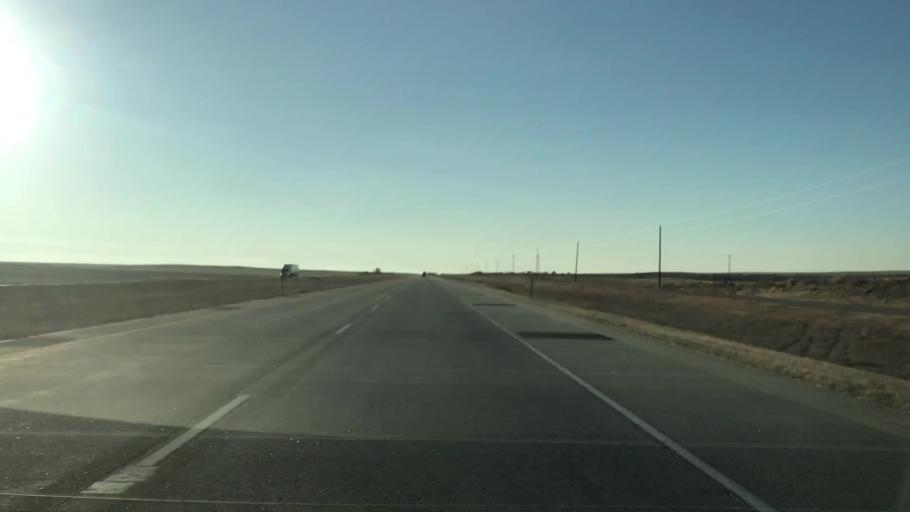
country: US
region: Colorado
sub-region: Arapahoe County
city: Byers
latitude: 39.5855
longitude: -104.0272
